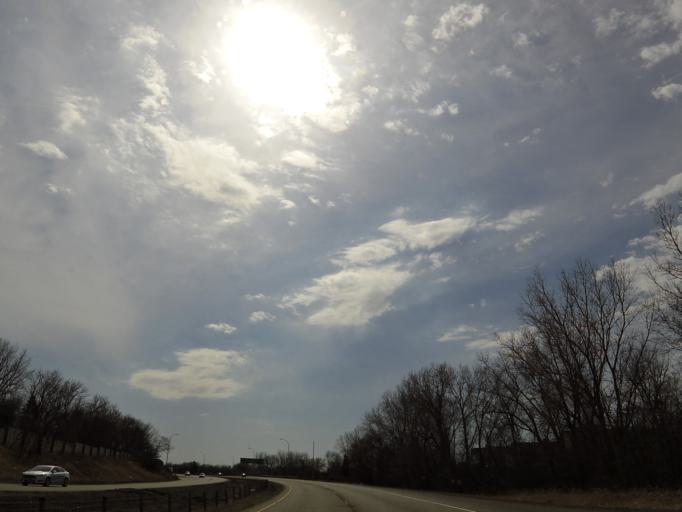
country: US
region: Minnesota
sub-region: Dakota County
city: South Saint Paul
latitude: 44.8893
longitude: -93.0665
